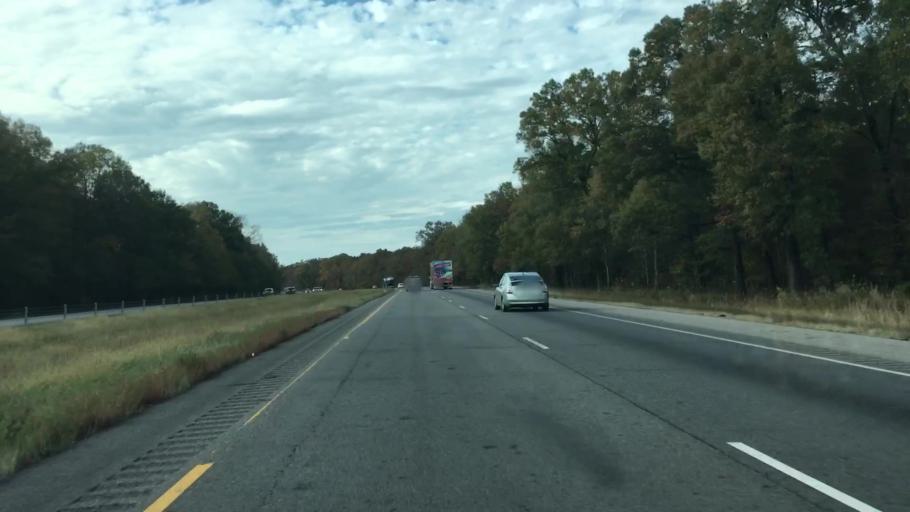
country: US
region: Arkansas
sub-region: Pope County
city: Atkins
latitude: 35.2431
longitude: -92.8617
